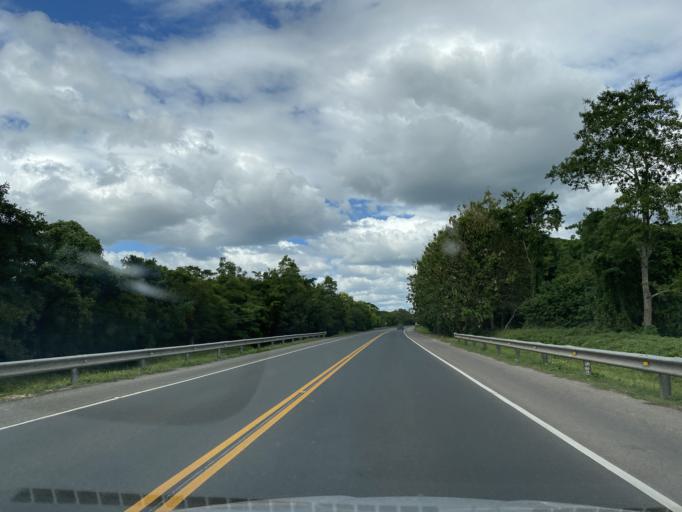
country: DO
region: Santo Domingo
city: Guerra
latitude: 18.5979
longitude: -69.7710
